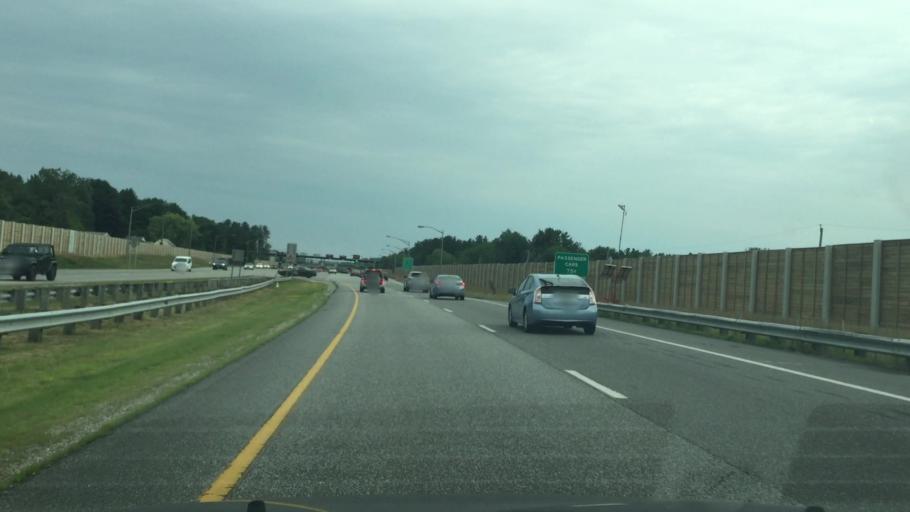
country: US
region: Maine
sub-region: York County
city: Eliot
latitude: 43.1397
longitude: -70.8428
